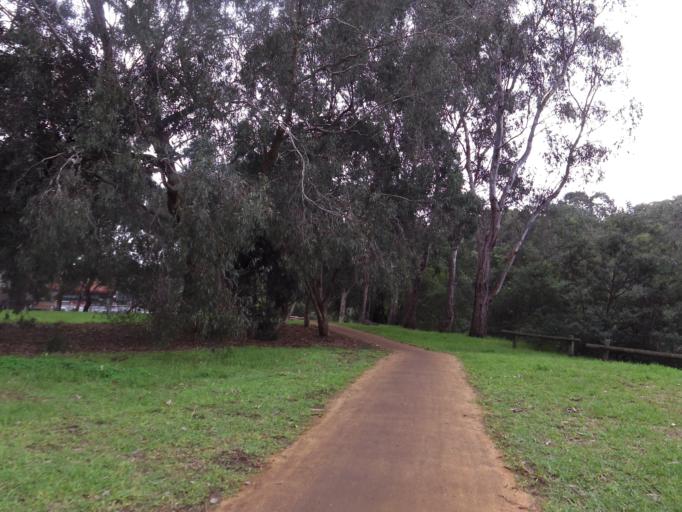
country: AU
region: Victoria
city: Abbotsford
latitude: -37.8081
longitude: 145.0085
